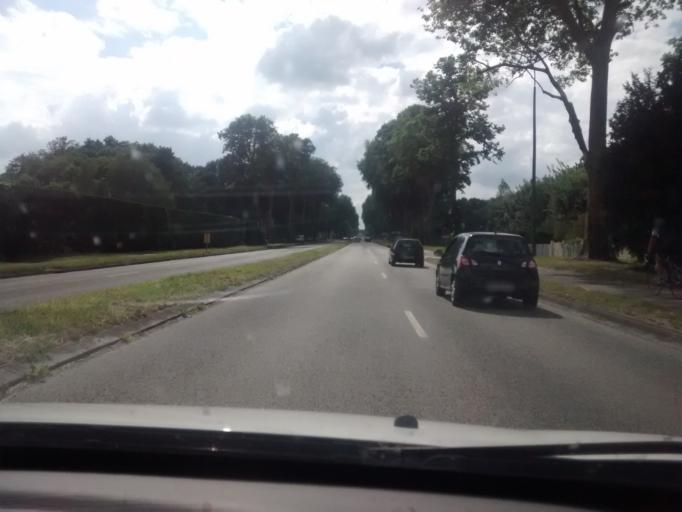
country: FR
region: Ile-de-France
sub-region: Departement des Yvelines
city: Saint-Cyr-l'Ecole
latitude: 48.8024
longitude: 2.0926
